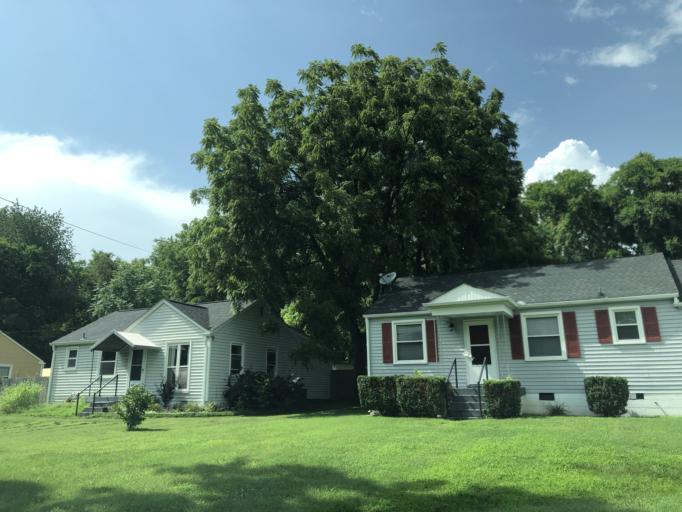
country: US
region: Tennessee
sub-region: Davidson County
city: Lakewood
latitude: 36.1715
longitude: -86.6744
